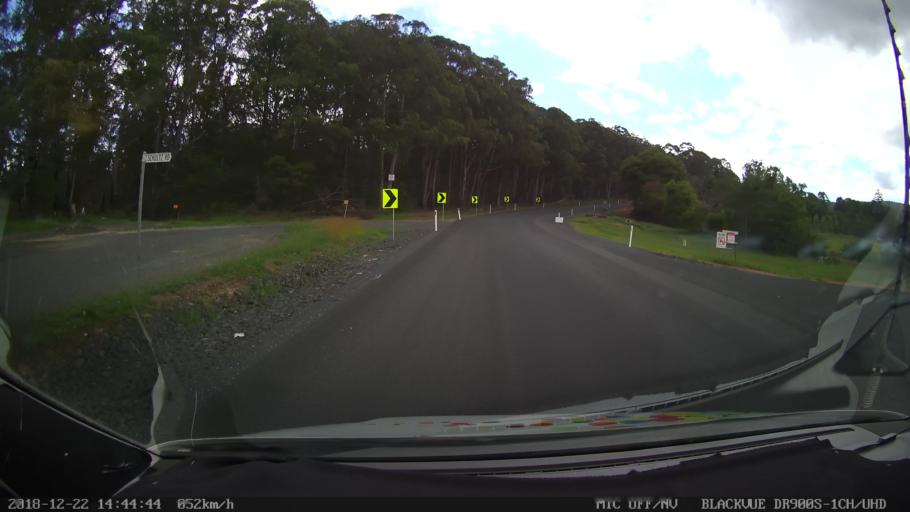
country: AU
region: New South Wales
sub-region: Bellingen
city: Dorrigo
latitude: -30.1669
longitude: 152.5745
